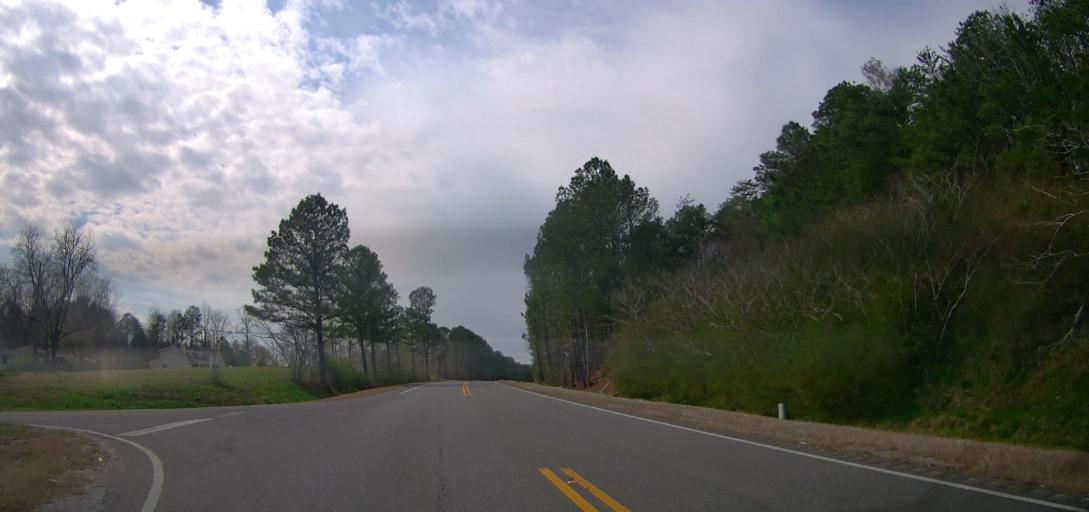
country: US
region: Alabama
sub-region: Walker County
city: Carbon Hill
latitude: 33.9184
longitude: -87.5779
